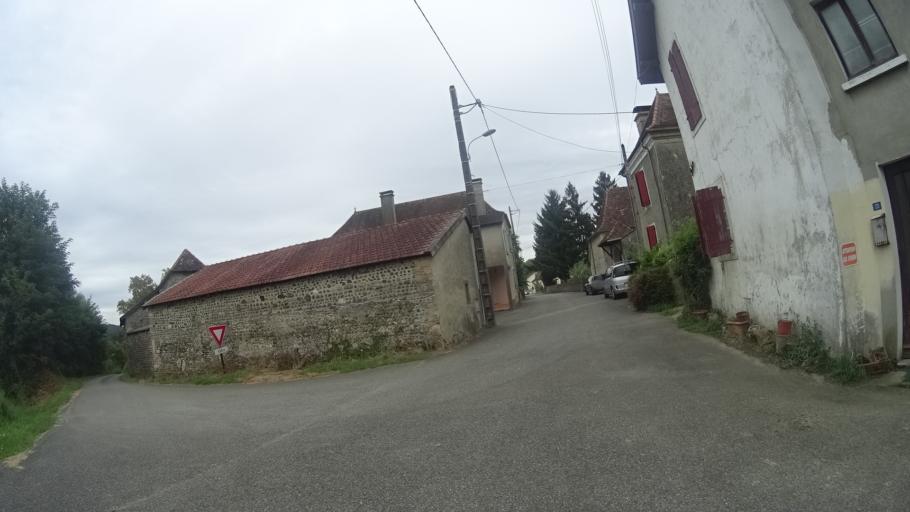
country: FR
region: Aquitaine
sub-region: Departement des Pyrenees-Atlantiques
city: Orthez
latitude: 43.4698
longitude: -0.7200
